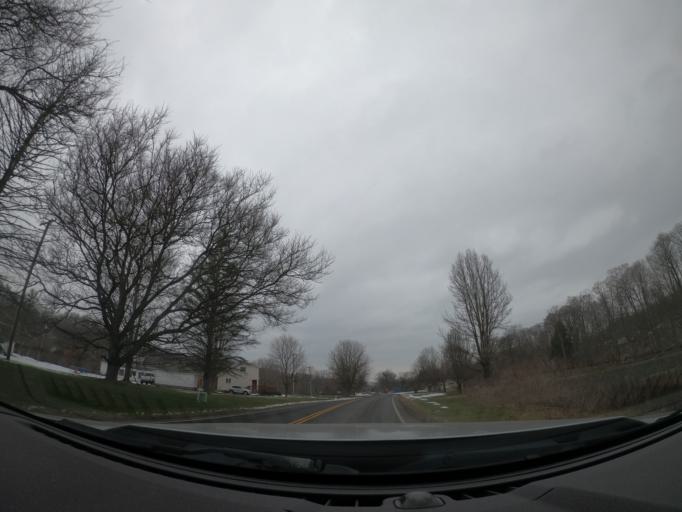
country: US
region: New York
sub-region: Cayuga County
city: Moravia
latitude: 42.6434
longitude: -76.4472
